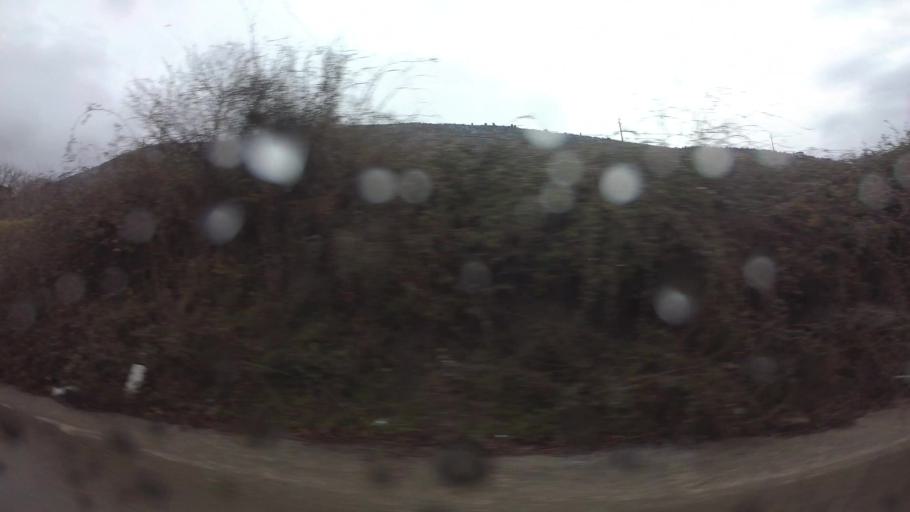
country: BA
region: Federation of Bosnia and Herzegovina
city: Blagaj
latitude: 43.2927
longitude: 17.8583
